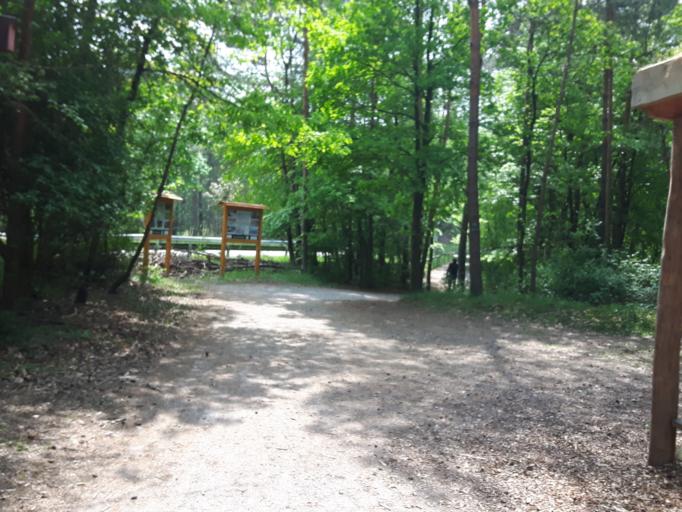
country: DE
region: North Rhine-Westphalia
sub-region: Regierungsbezirk Detmold
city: Augustdorf
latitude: 51.8570
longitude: 8.6990
